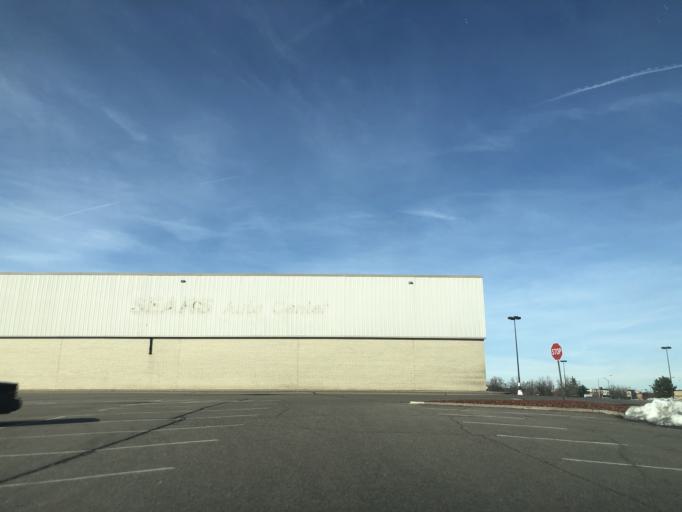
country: US
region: Colorado
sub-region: Adams County
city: Aurora
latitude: 39.7087
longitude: -104.8206
